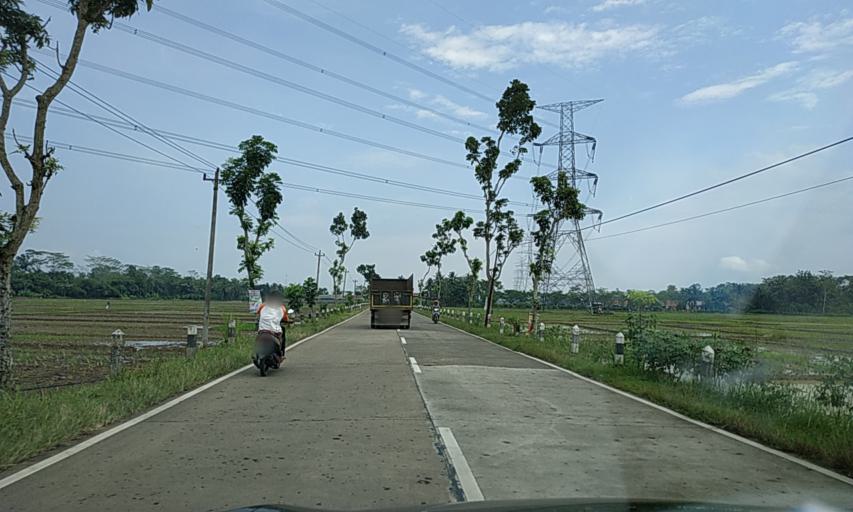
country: ID
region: Central Java
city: Tambangan
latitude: -7.4829
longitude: 108.8295
